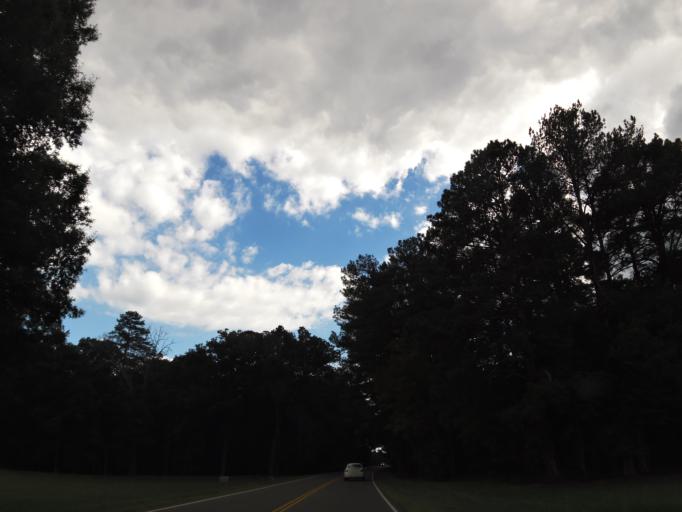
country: US
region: Georgia
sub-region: Catoosa County
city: Fort Oglethorpe
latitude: 34.9282
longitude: -85.2598
